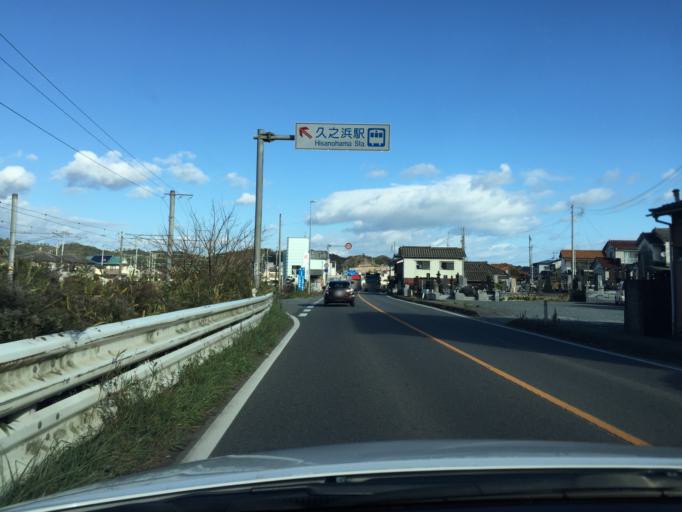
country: JP
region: Fukushima
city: Iwaki
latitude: 37.1380
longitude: 140.9967
